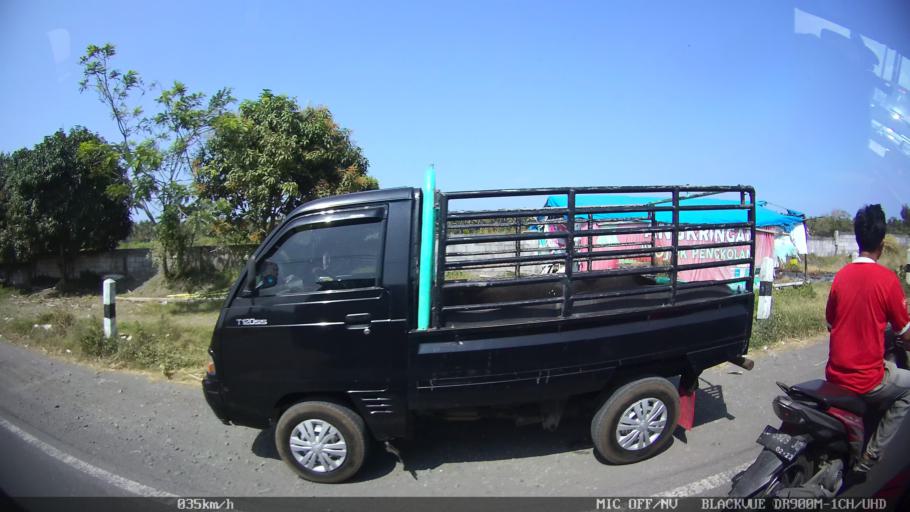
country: ID
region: Daerah Istimewa Yogyakarta
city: Srandakan
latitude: -7.9523
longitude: 110.1916
